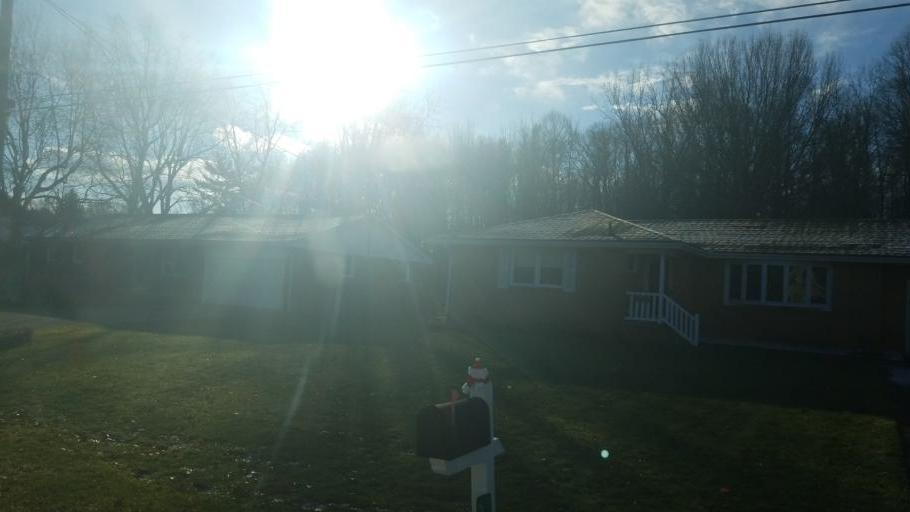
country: US
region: Ohio
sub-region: Richland County
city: Ontario
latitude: 40.7571
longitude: -82.5936
